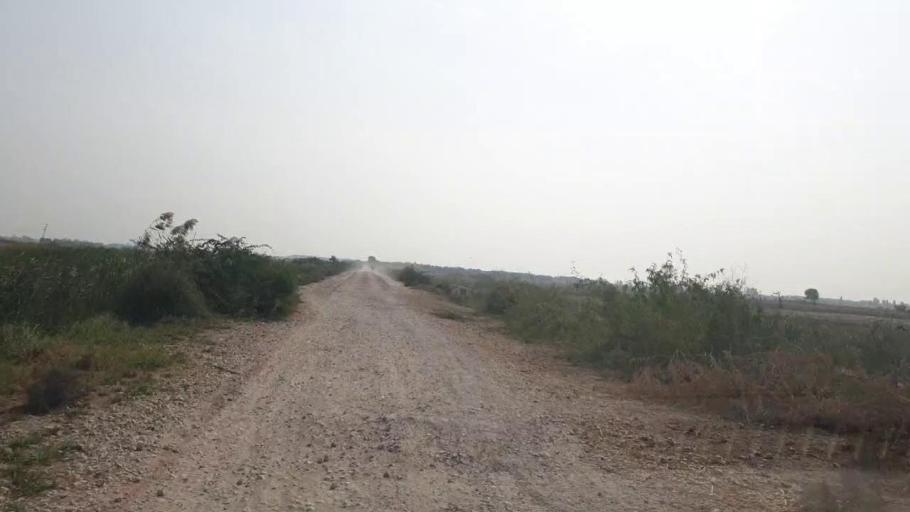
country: PK
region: Sindh
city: Tando Muhammad Khan
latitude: 25.0486
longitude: 68.3891
